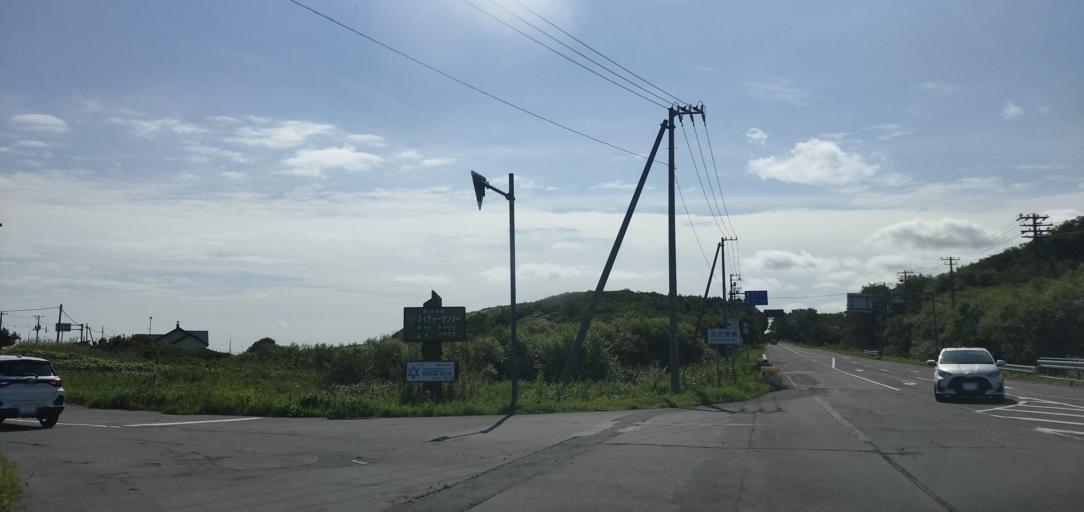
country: JP
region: Hokkaido
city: Shibetsu
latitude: 43.6384
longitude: 145.1629
